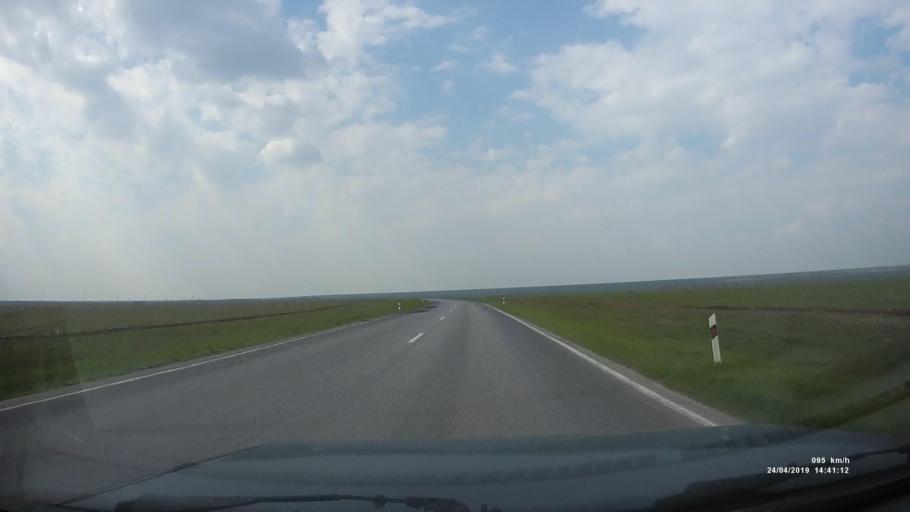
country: RU
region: Rostov
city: Remontnoye
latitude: 46.4426
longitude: 43.8826
